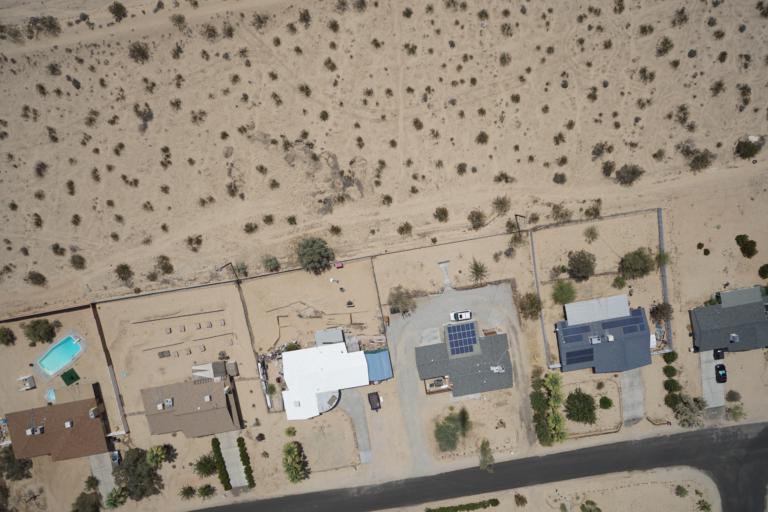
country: US
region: California
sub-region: San Bernardino County
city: Twentynine Palms
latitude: 34.1531
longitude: -116.0469
